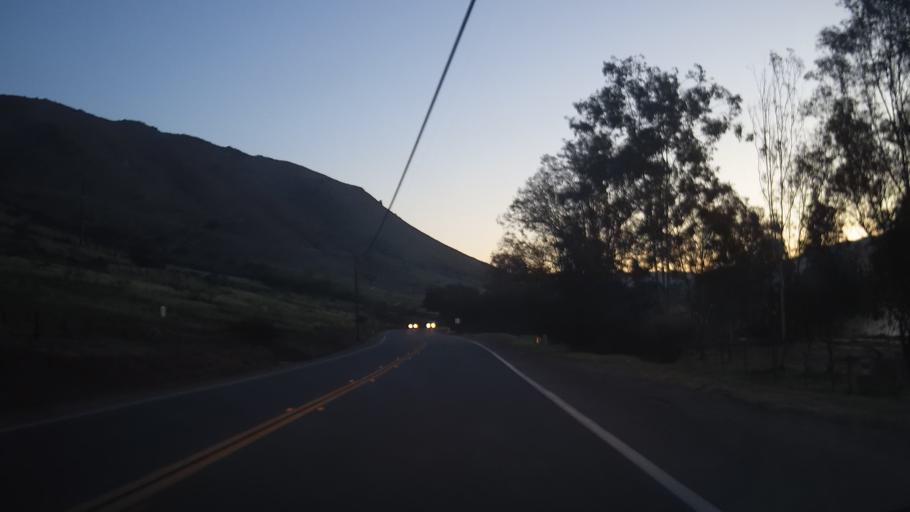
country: US
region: California
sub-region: San Diego County
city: Crest
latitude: 32.7808
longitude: -116.8608
